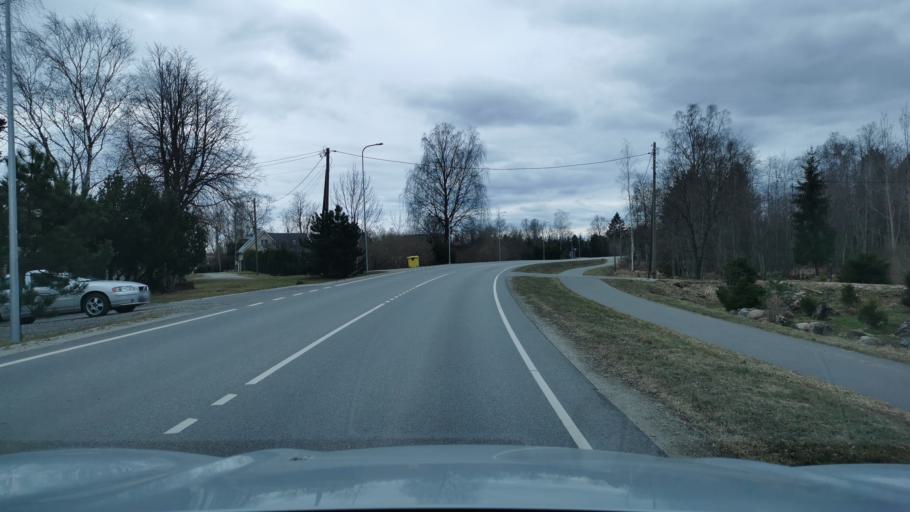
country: EE
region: Ida-Virumaa
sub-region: Puessi linn
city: Pussi
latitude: 59.3446
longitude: 27.0158
